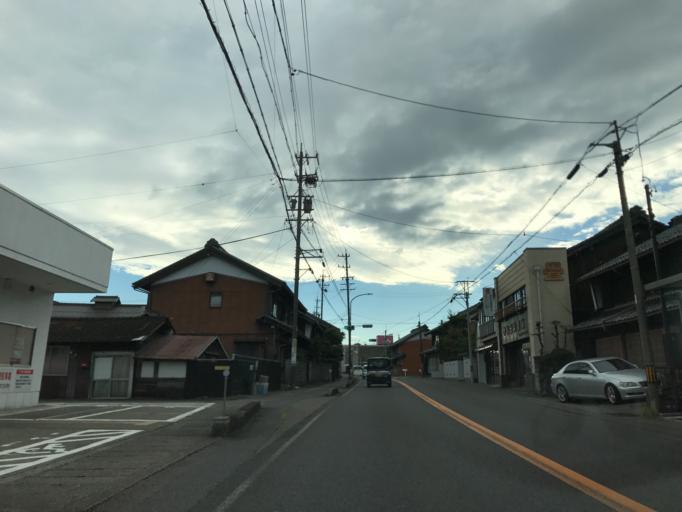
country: JP
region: Gifu
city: Tarui
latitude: 35.3630
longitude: 136.4737
